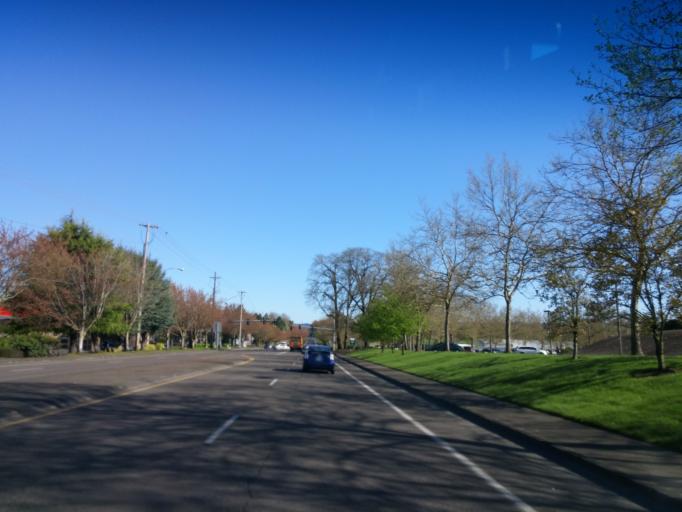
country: US
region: Oregon
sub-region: Washington County
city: Oak Hills
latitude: 45.5186
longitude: -122.8395
